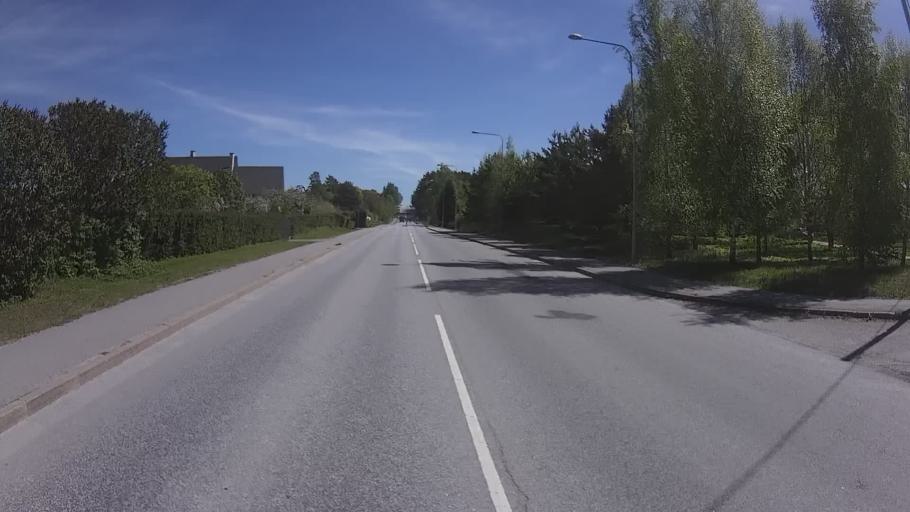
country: EE
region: Vorumaa
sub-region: Voru linn
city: Voru
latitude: 57.8138
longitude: 27.0412
